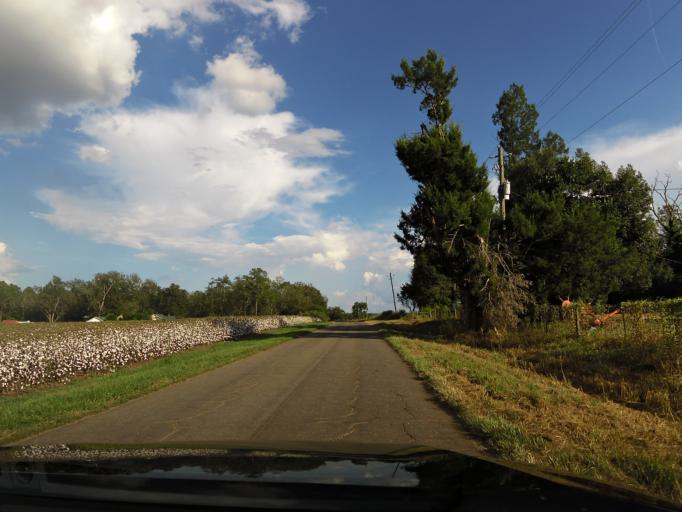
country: US
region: Georgia
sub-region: Brooks County
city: Quitman
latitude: 30.7801
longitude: -83.6180
